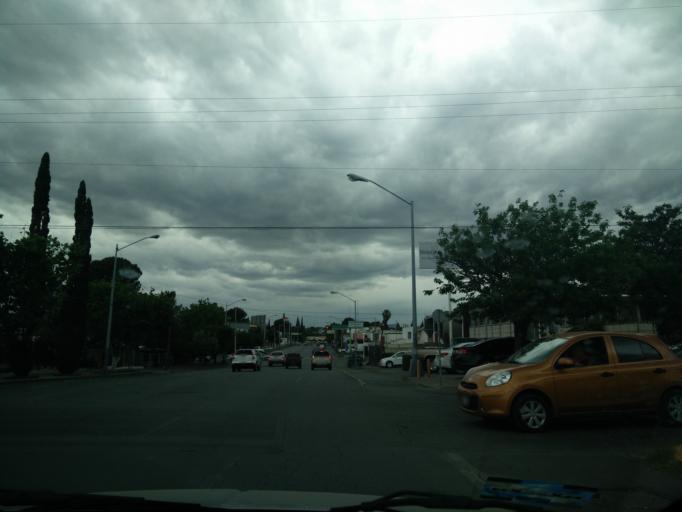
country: MX
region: Chihuahua
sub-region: Chihuahua
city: Chihuahua
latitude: 28.6491
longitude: -106.0881
